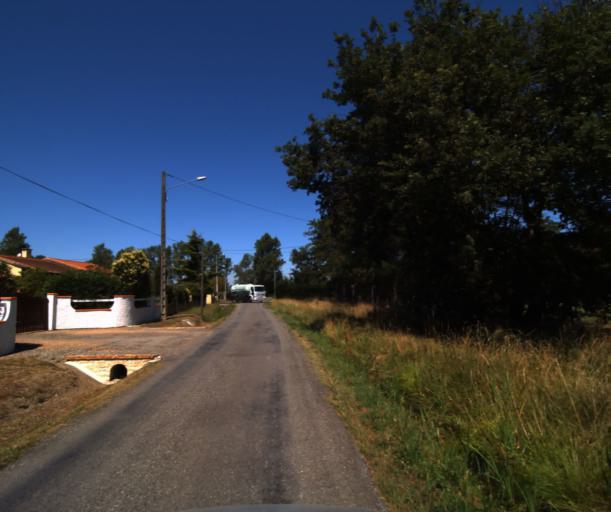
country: FR
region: Midi-Pyrenees
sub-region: Departement de la Haute-Garonne
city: Seysses
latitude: 43.4773
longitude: 1.2920
